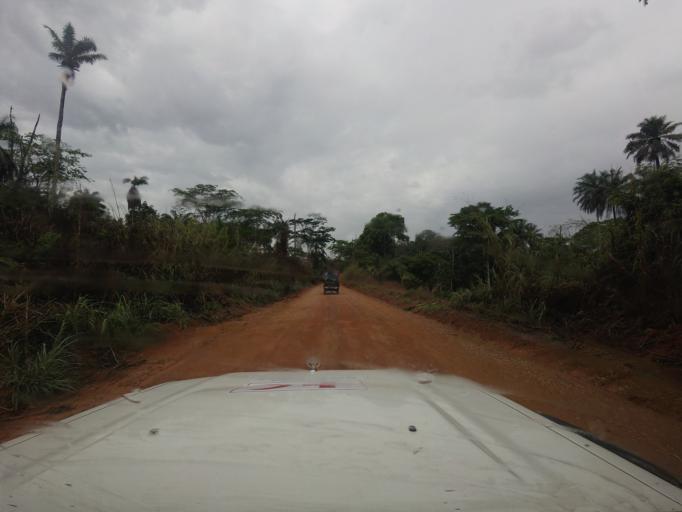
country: SL
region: Eastern Province
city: Buedu
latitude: 8.3182
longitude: -10.1535
